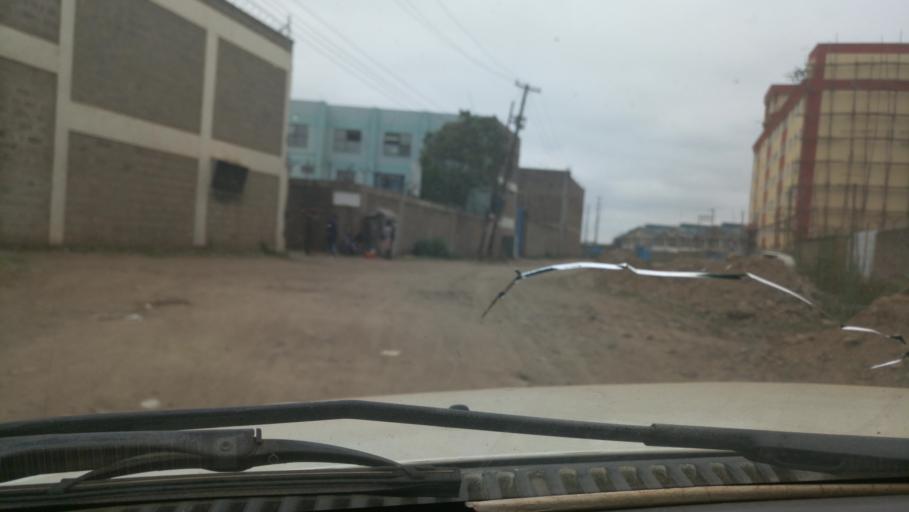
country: KE
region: Nairobi Area
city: Pumwani
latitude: -1.3346
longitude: 36.8677
